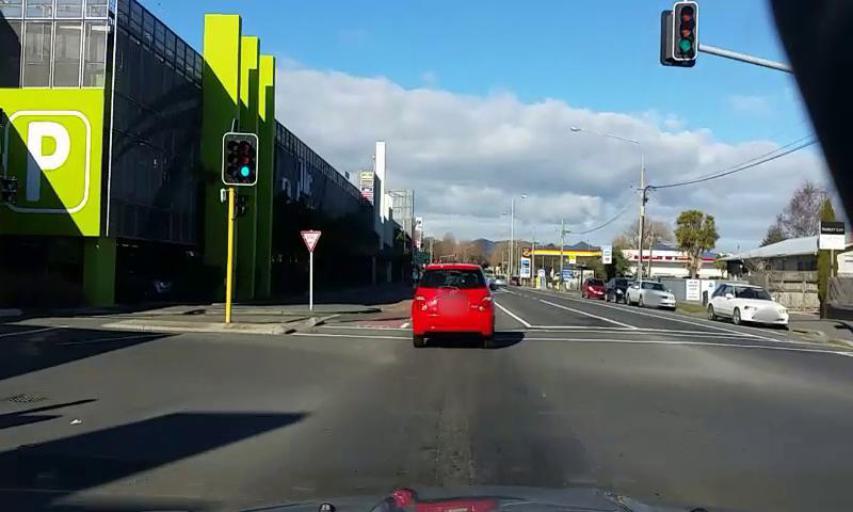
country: NZ
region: Canterbury
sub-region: Christchurch City
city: Christchurch
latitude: -43.5060
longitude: 172.6627
